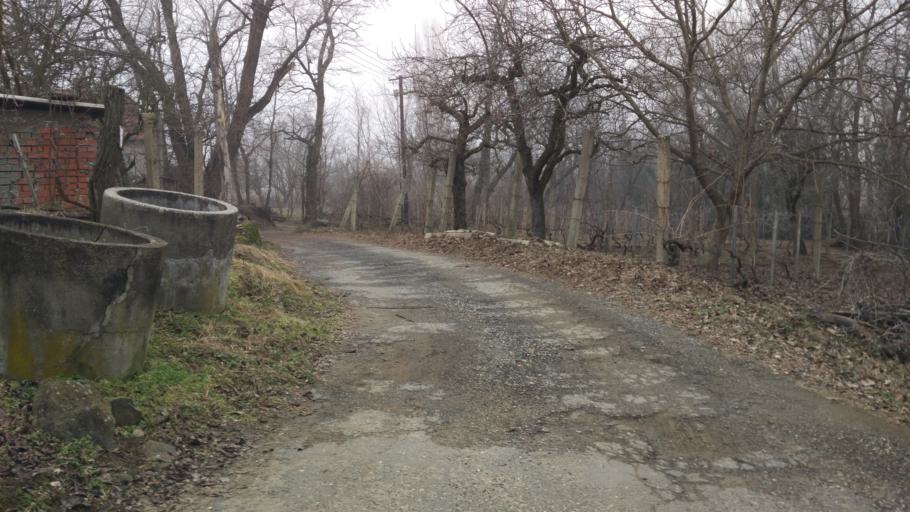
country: HU
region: Veszprem
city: Badacsonytomaj
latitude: 46.8143
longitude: 17.4945
